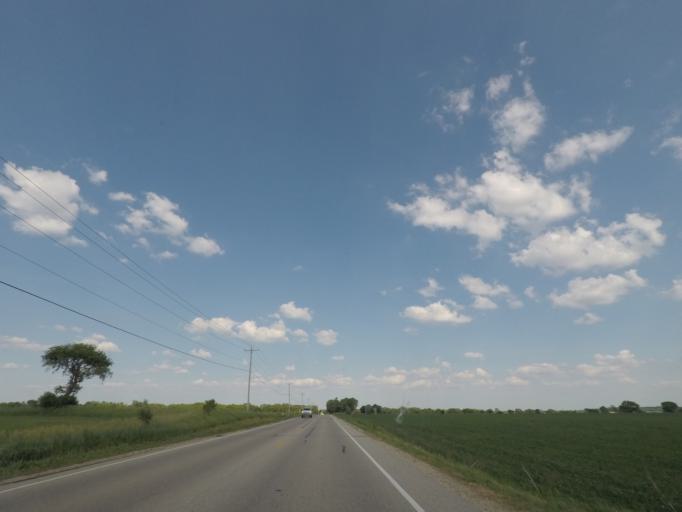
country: US
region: Wisconsin
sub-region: Walworth County
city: East Troy
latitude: 42.7926
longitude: -88.4405
